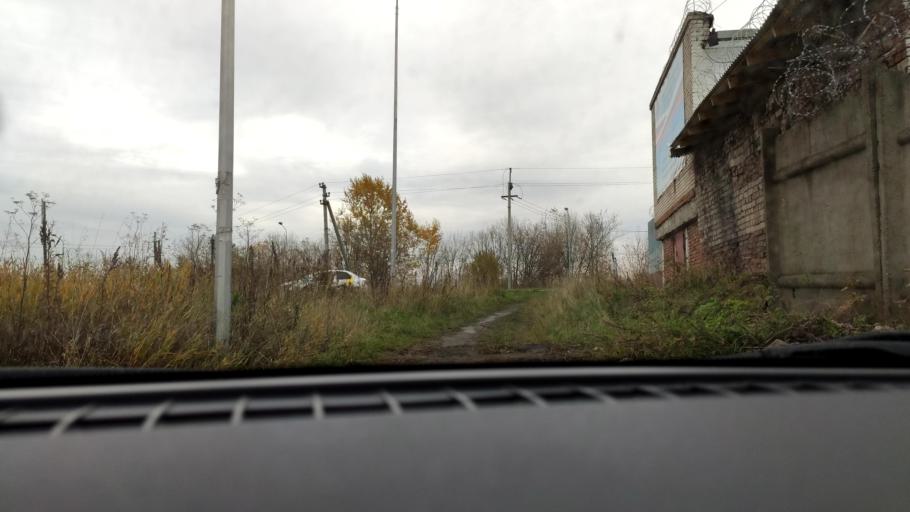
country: RU
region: Perm
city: Perm
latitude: 57.9781
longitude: 56.2829
